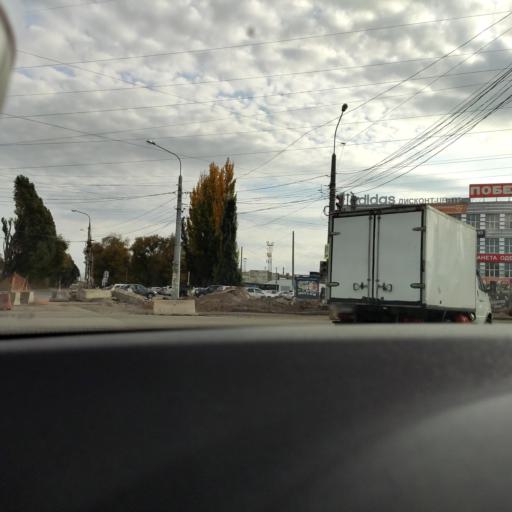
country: RU
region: Samara
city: Samara
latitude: 53.1958
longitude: 50.2481
